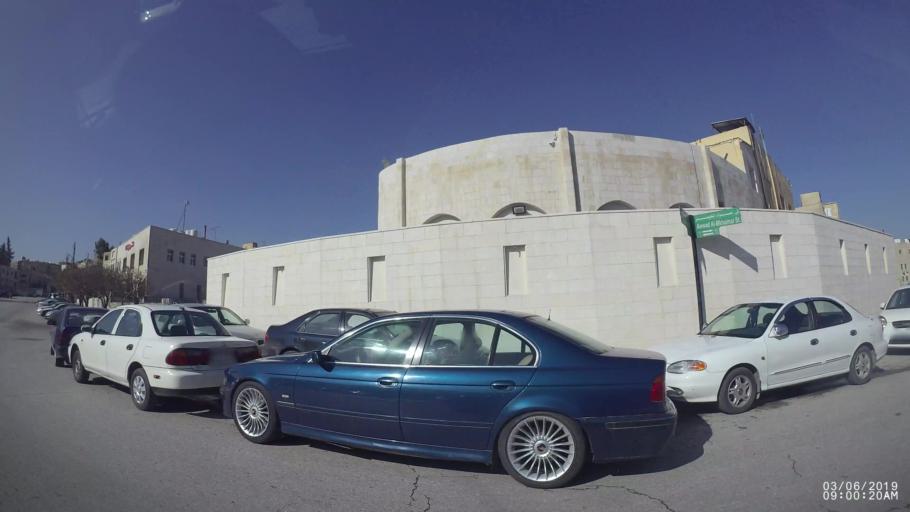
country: JO
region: Amman
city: Amman
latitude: 31.9871
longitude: 35.9935
